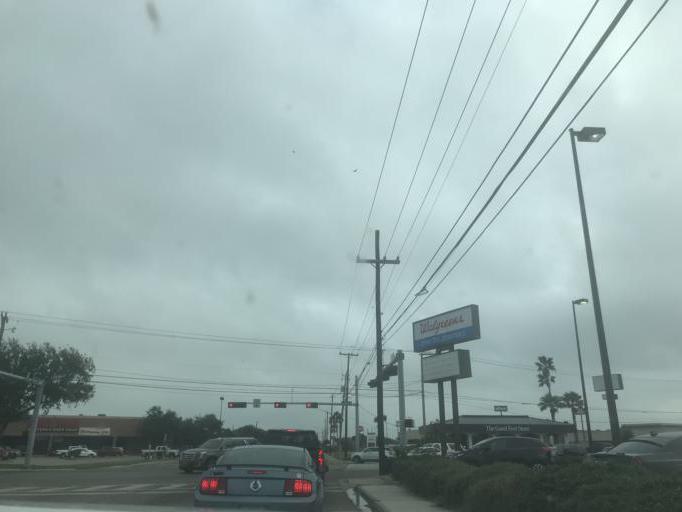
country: US
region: Texas
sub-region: Nueces County
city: Corpus Christi
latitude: 27.7084
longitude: -97.3630
